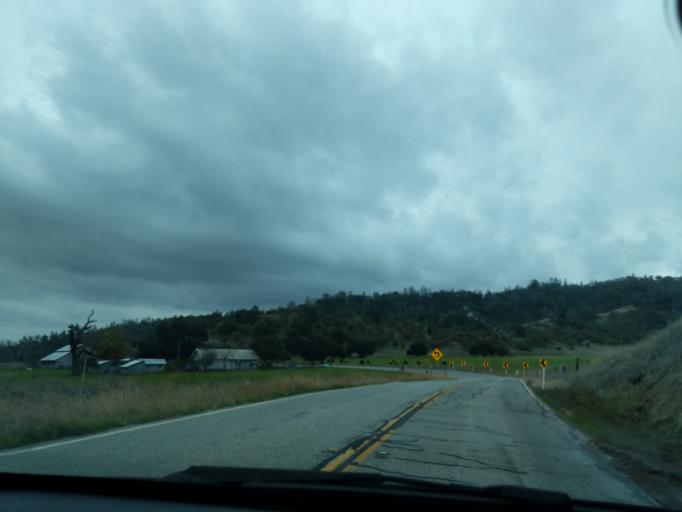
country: US
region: California
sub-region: Monterey County
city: Soledad
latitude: 36.5690
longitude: -121.1842
